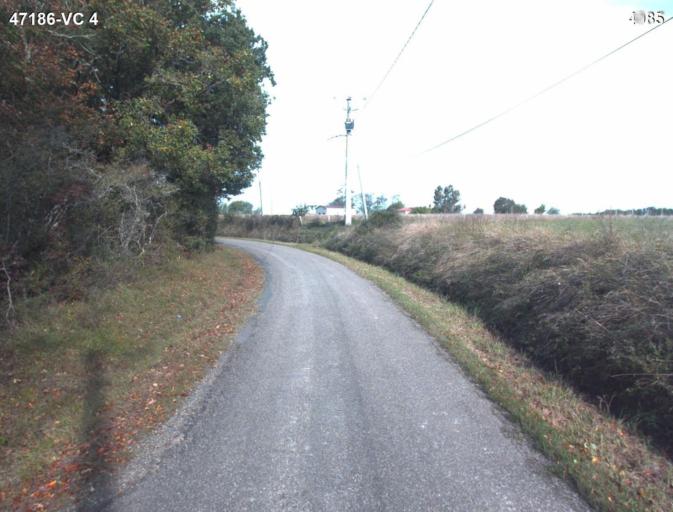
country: FR
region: Aquitaine
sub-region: Departement du Lot-et-Garonne
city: Sainte-Colombe-en-Bruilhois
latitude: 44.1910
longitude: 0.4569
